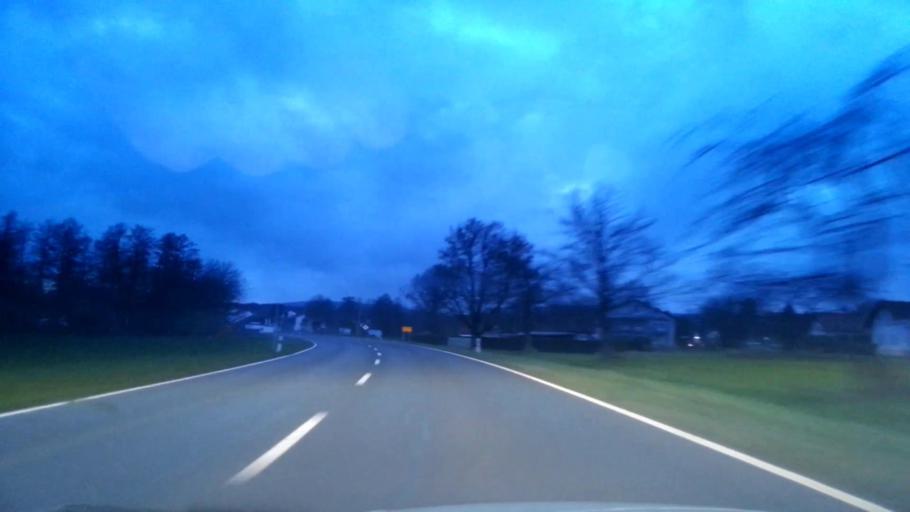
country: DE
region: Bavaria
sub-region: Upper Palatinate
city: Immenreuth
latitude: 49.9026
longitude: 11.8713
